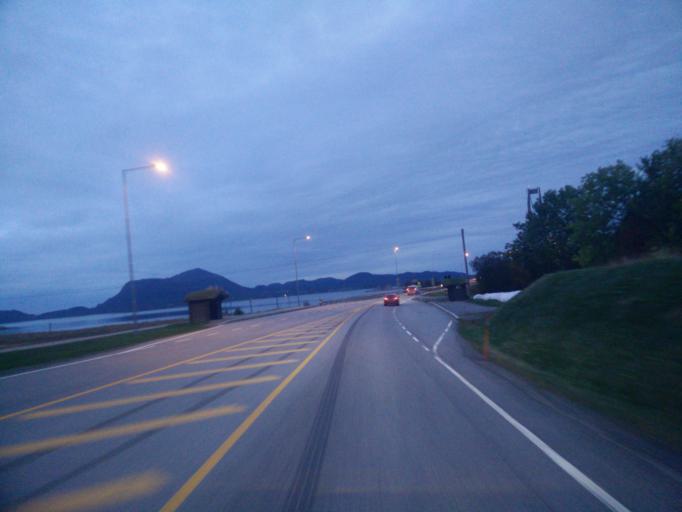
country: NO
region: More og Romsdal
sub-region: Gjemnes
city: Batnfjordsora
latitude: 62.9639
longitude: 7.7688
